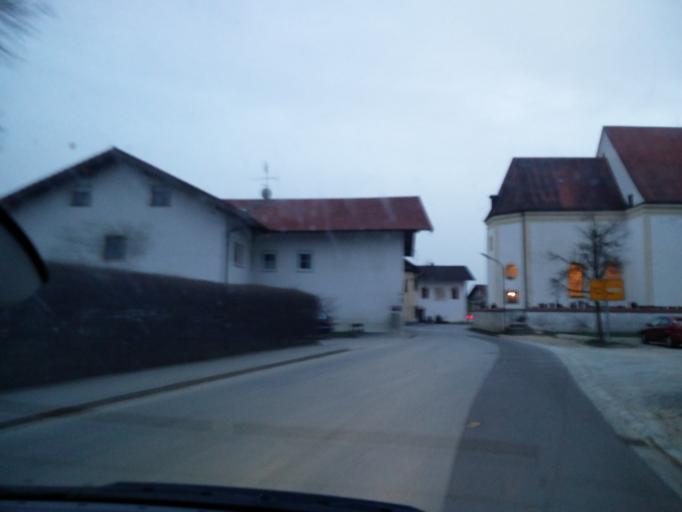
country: DE
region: Bavaria
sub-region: Upper Bavaria
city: Albaching
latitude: 48.1119
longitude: 12.1111
